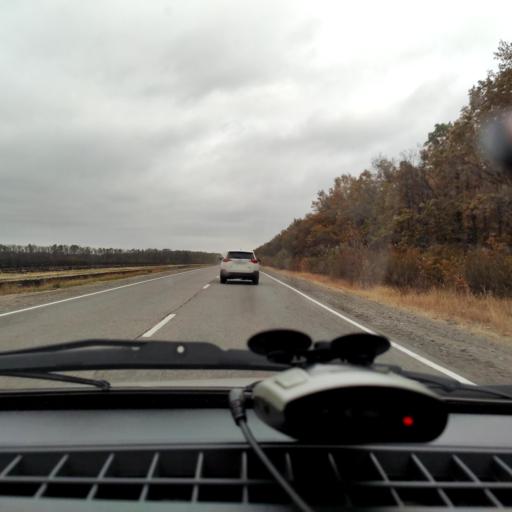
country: RU
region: Voronezj
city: Shilovo
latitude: 51.4206
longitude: 39.0072
